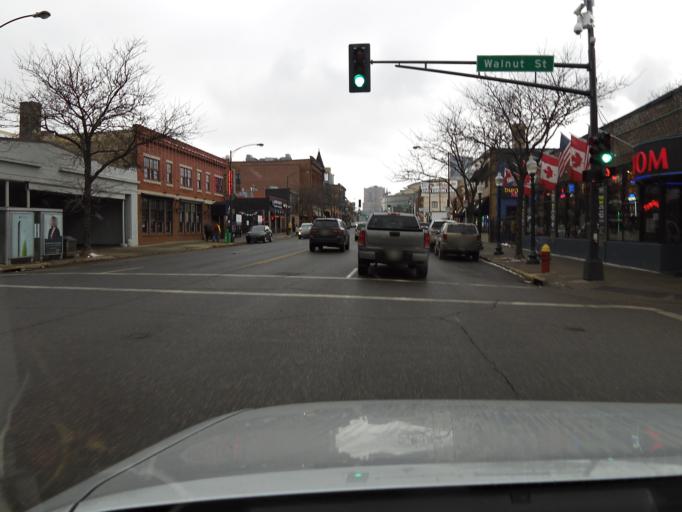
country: US
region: Minnesota
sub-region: Ramsey County
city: Saint Paul
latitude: 44.9425
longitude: -93.1052
